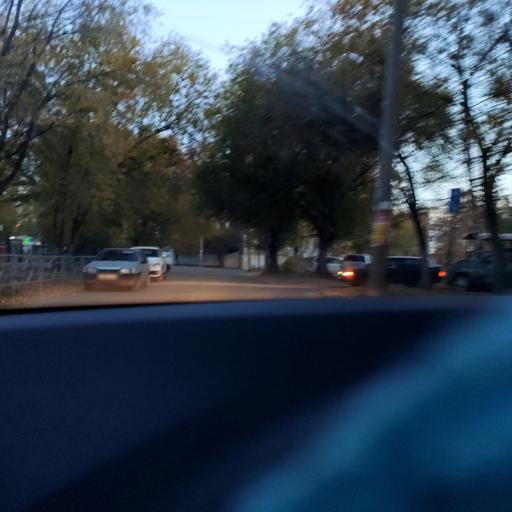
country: RU
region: Samara
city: Samara
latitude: 53.2541
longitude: 50.2393
